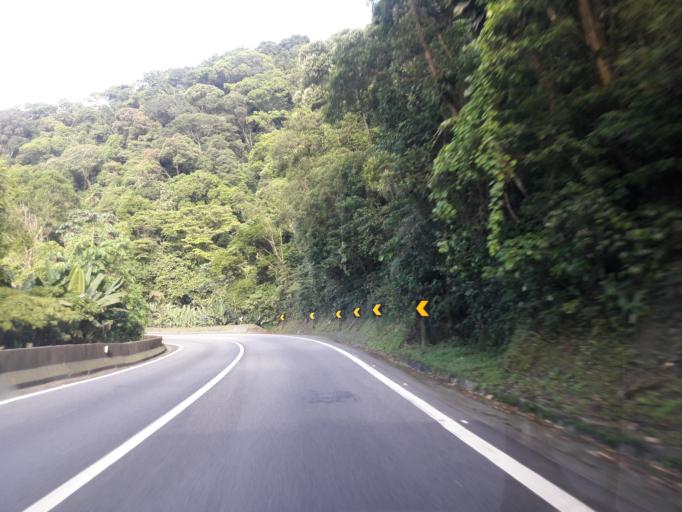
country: BR
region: Sao Paulo
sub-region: Cubatao
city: Cubatao
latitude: -23.8884
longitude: -46.4876
